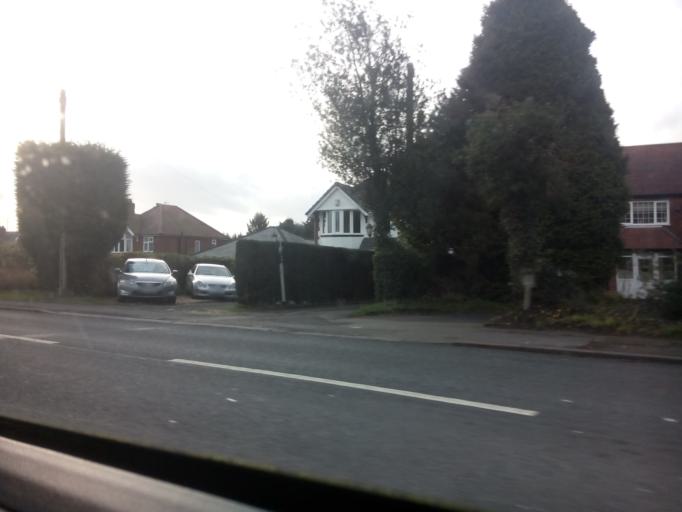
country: GB
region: England
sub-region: Worcestershire
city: Bromsgrove
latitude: 52.3702
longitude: -2.0460
